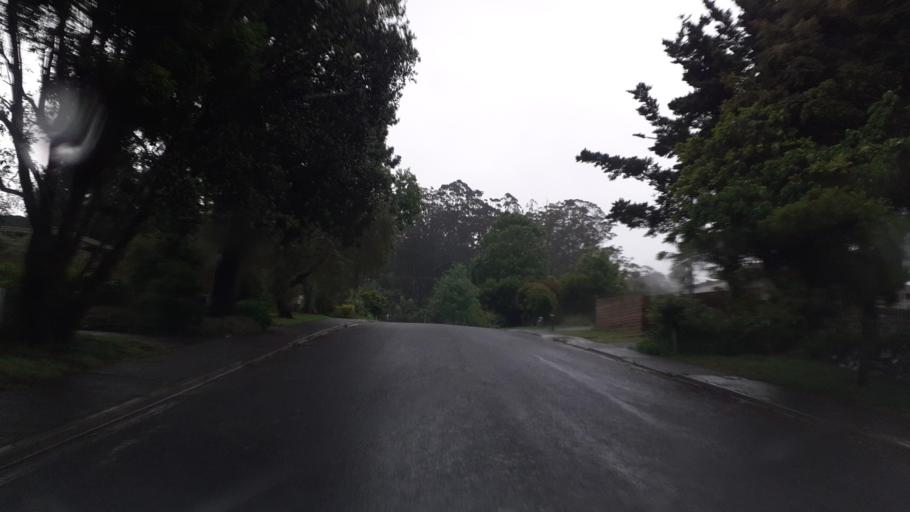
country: NZ
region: Northland
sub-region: Far North District
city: Kerikeri
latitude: -35.2237
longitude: 173.9539
